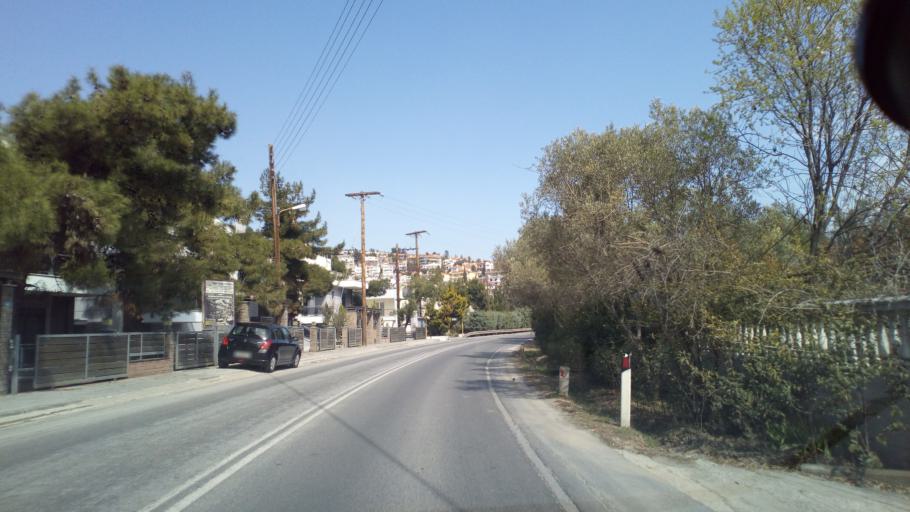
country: GR
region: Central Macedonia
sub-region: Nomos Thessalonikis
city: Panorama
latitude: 40.5792
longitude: 23.0272
